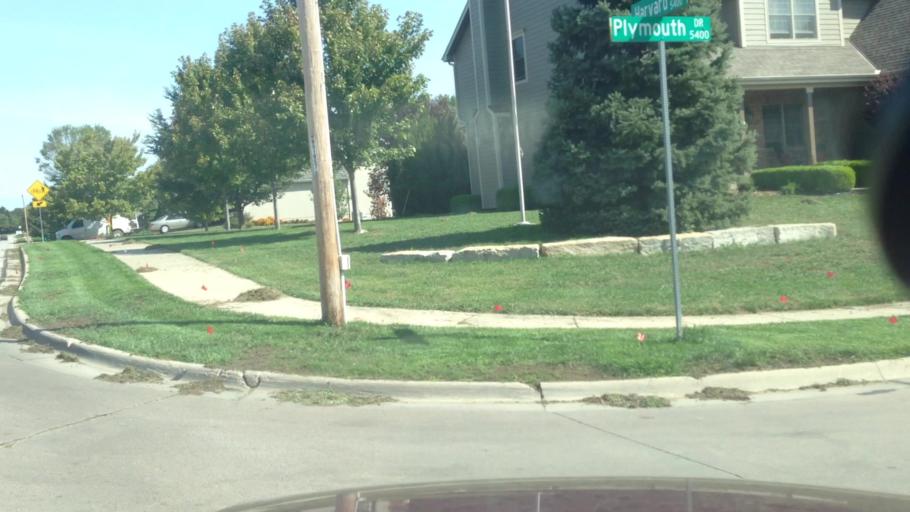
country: US
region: Kansas
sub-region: Douglas County
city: Lawrence
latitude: 38.9642
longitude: -95.3174
